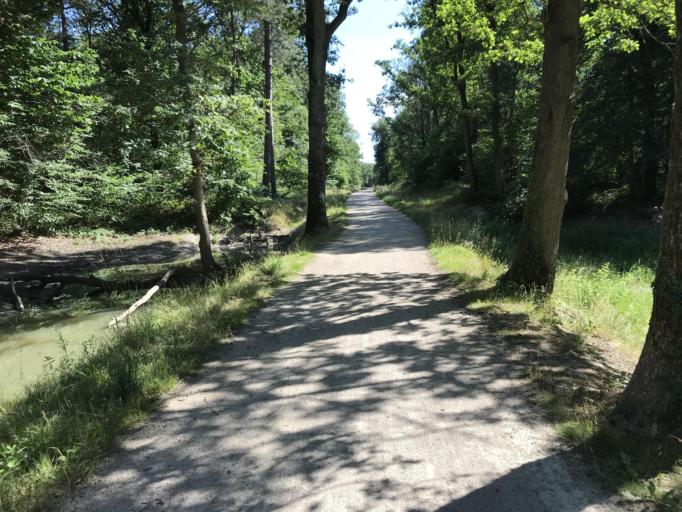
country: FR
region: Ile-de-France
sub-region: Departement de l'Essonne
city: Bondoufle
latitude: 48.6308
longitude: 2.3837
